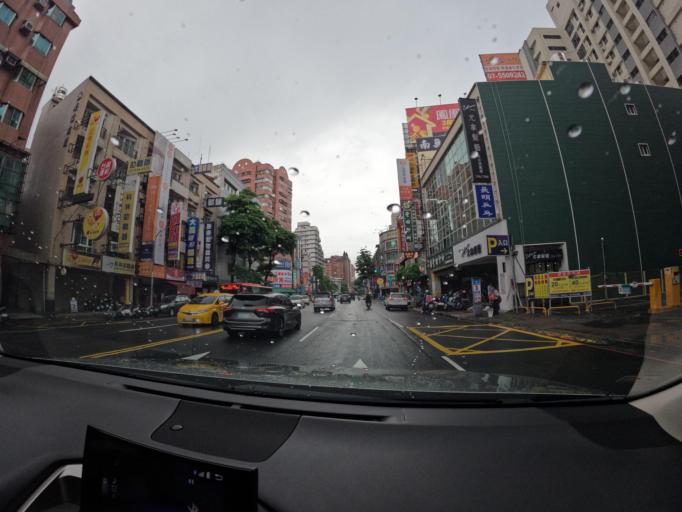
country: TW
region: Kaohsiung
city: Kaohsiung
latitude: 22.6635
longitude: 120.3082
